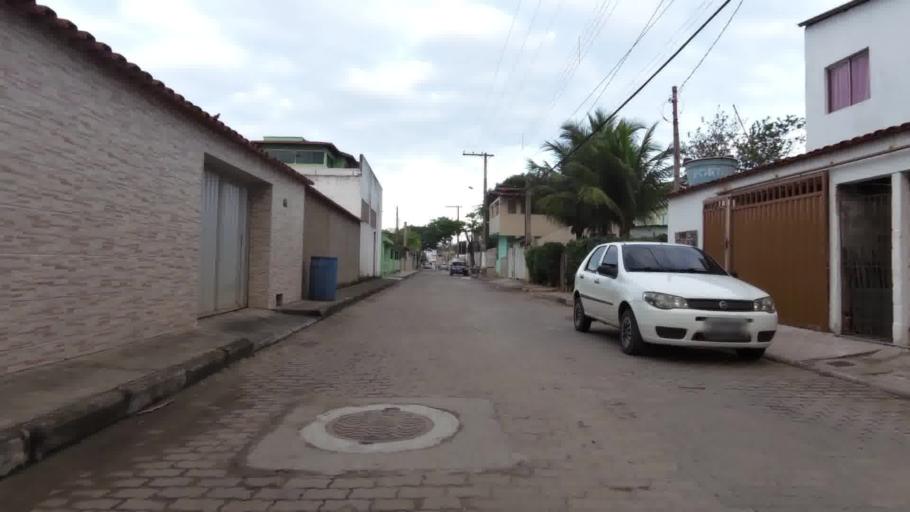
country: BR
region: Espirito Santo
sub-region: Piuma
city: Piuma
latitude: -20.8096
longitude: -40.6360
